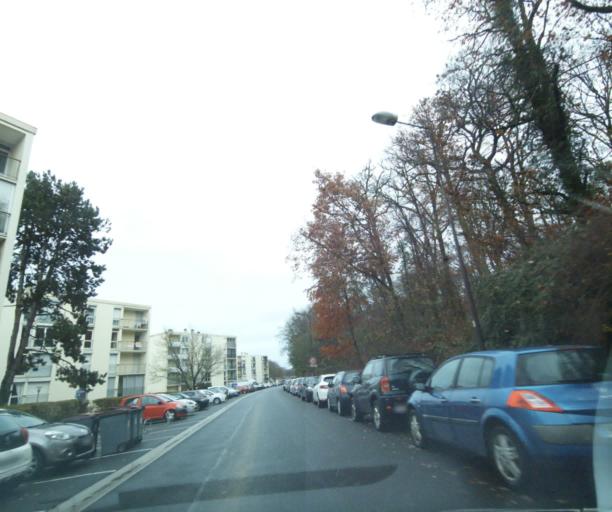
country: FR
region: Ile-de-France
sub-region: Departement de Seine-et-Marne
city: Avon
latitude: 48.4098
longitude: 2.7371
